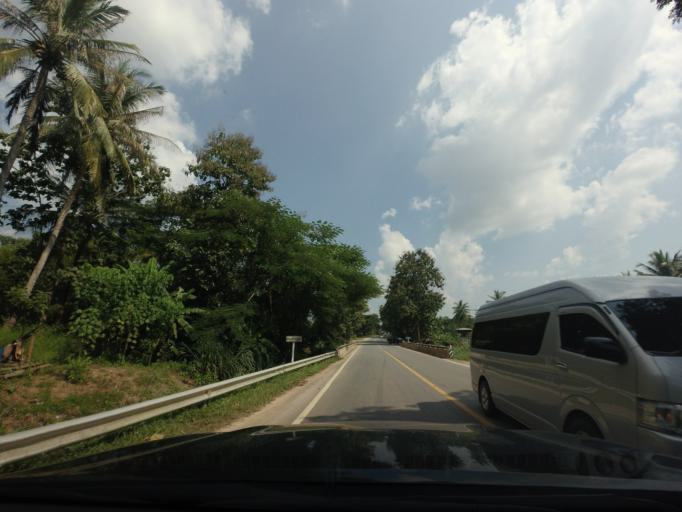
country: TH
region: Phitsanulok
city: Chat Trakan
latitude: 17.2918
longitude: 100.5133
